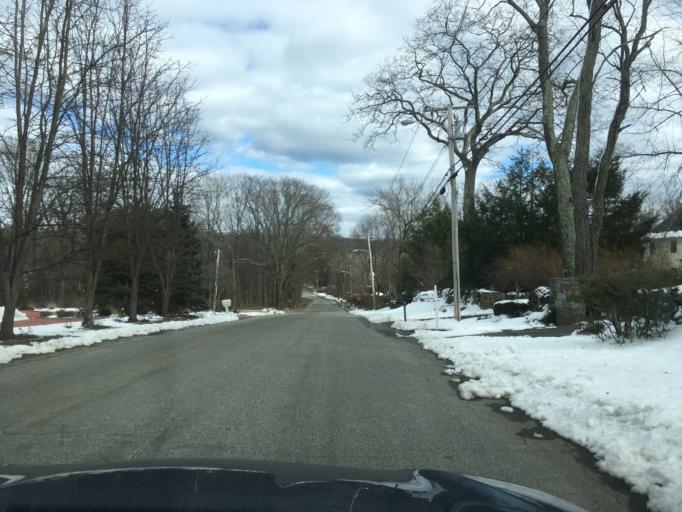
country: US
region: Rhode Island
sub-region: Kent County
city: East Greenwich
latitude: 41.6734
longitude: -71.4714
